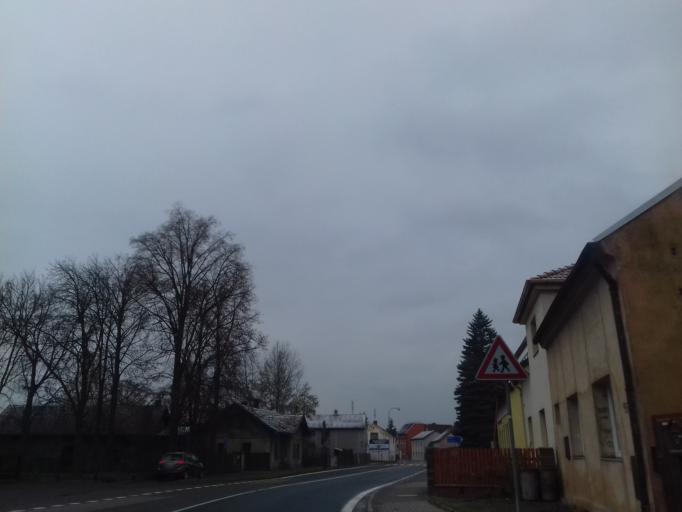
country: CZ
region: Plzensky
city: Stankov
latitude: 49.5568
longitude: 13.0728
